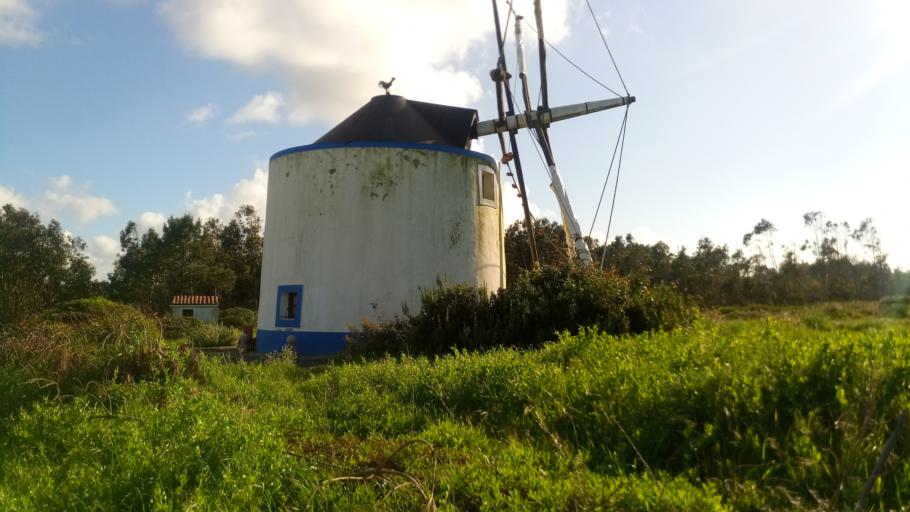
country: PT
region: Leiria
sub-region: Caldas da Rainha
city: Caldas da Rainha
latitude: 39.4582
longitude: -9.1955
